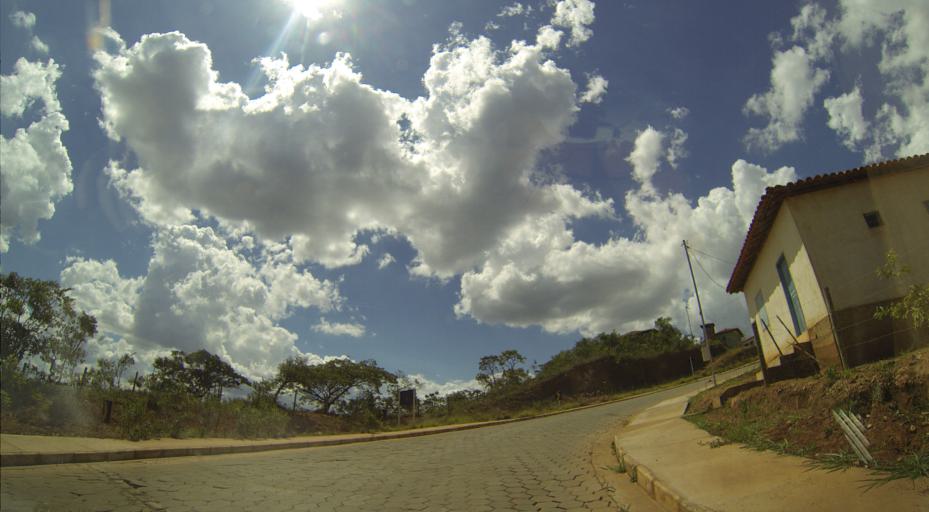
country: BR
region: Minas Gerais
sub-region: Serro
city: Serro
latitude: -18.4789
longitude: -43.4972
